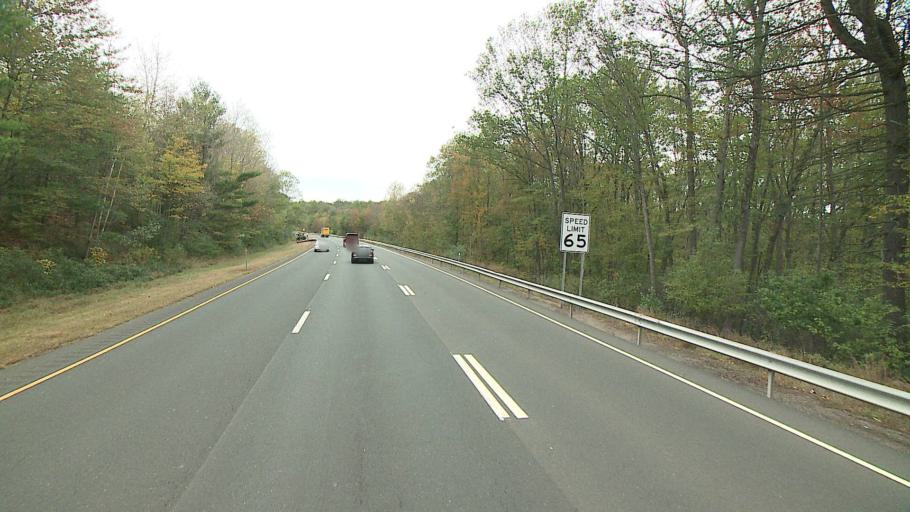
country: US
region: Connecticut
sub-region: Middlesex County
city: Higganum
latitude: 41.4622
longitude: -72.5355
